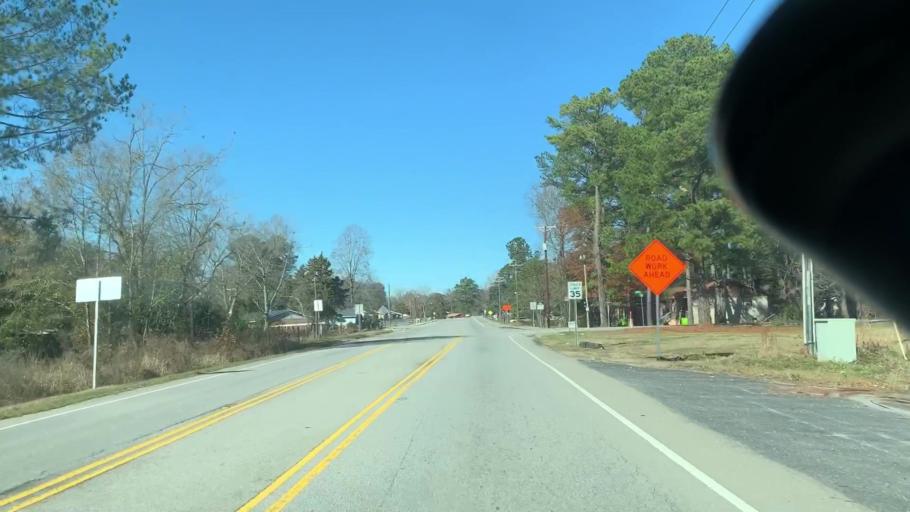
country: US
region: South Carolina
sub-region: Richland County
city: Forest Acres
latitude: 33.9318
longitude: -80.9686
